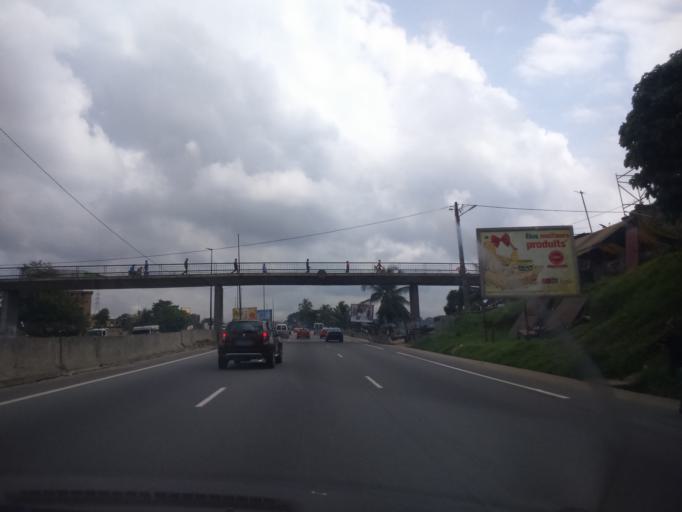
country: CI
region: Lagunes
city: Abobo
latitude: 5.3633
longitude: -4.0249
